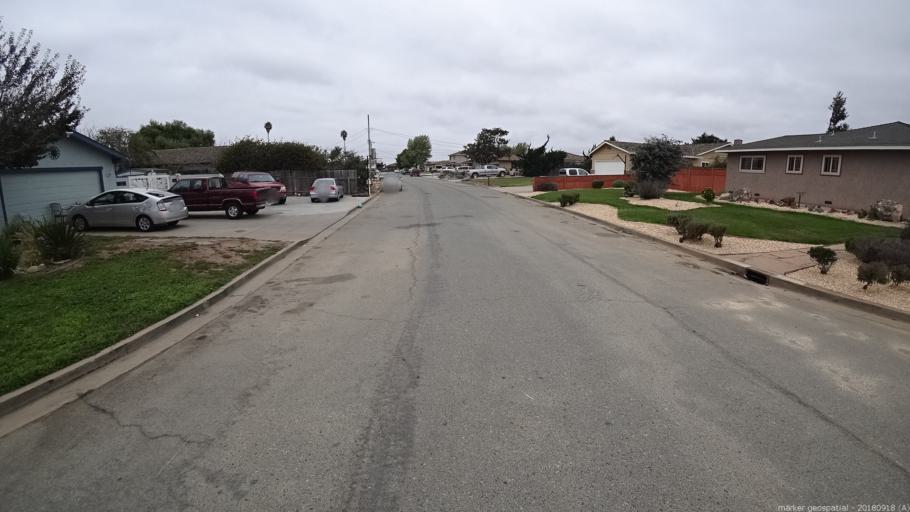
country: US
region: California
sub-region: Monterey County
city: Prunedale
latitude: 36.7369
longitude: -121.6389
